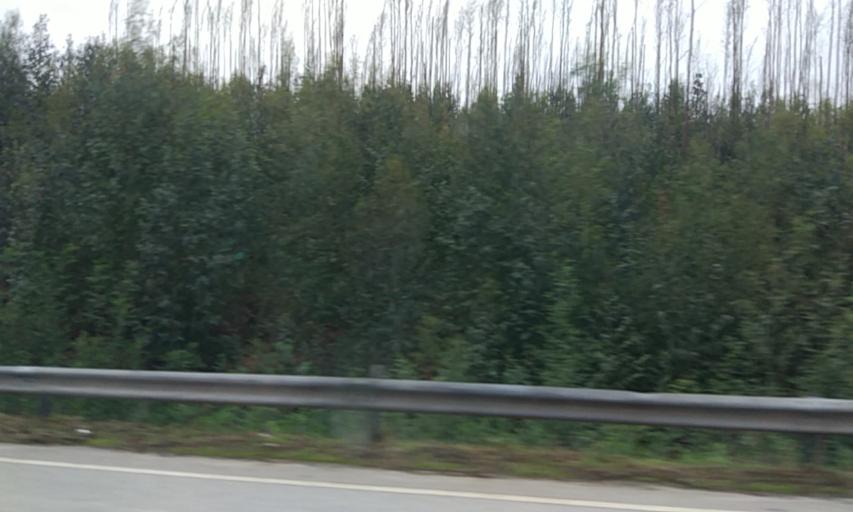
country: PT
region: Viseu
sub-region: Mortagua
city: Mortagua
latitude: 40.3553
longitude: -8.1948
